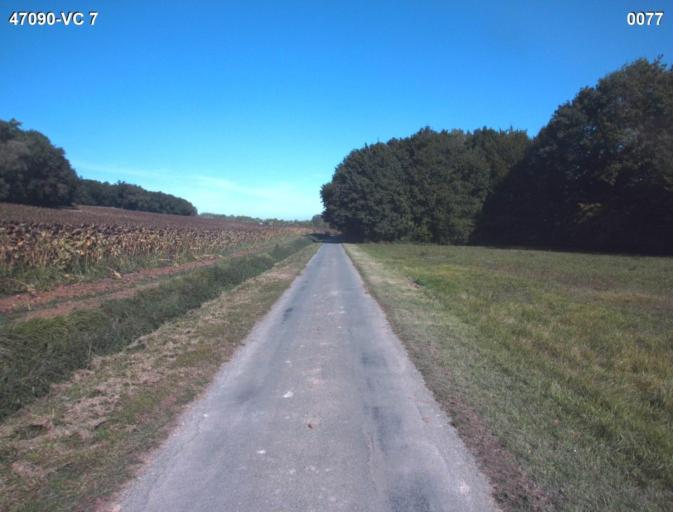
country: FR
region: Aquitaine
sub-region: Departement du Lot-et-Garonne
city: Nerac
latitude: 44.1675
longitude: 0.3629
